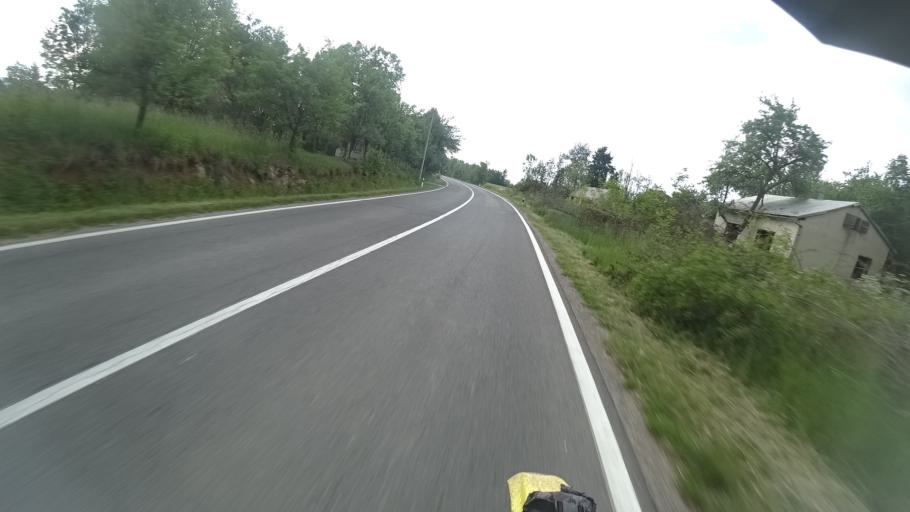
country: HR
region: Licko-Senjska
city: Gospic
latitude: 44.4968
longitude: 15.4583
